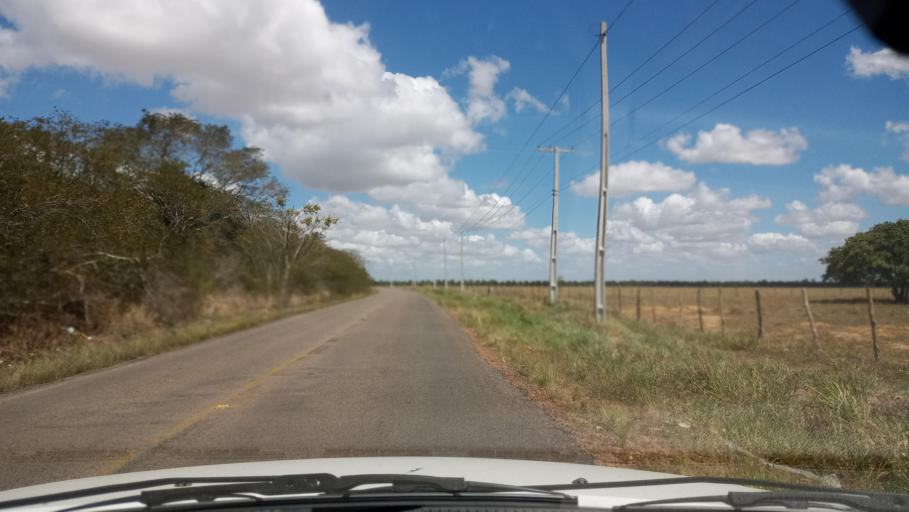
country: BR
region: Rio Grande do Norte
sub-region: Brejinho
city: Brejinho
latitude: -6.0410
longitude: -35.4140
